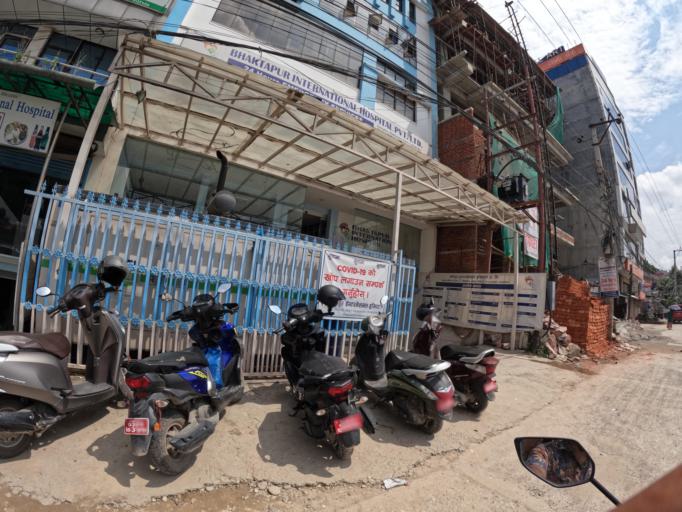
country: NP
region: Central Region
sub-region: Bagmati Zone
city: Patan
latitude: 27.6746
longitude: 85.3665
